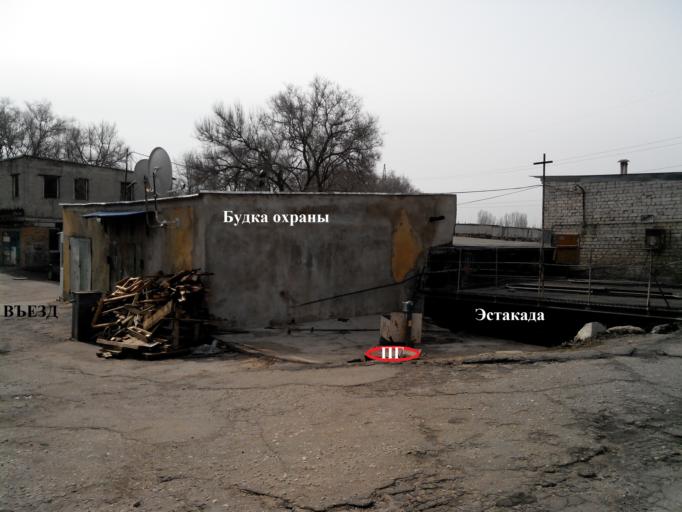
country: RU
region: Voronezj
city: Voronezh
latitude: 51.6375
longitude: 39.1546
